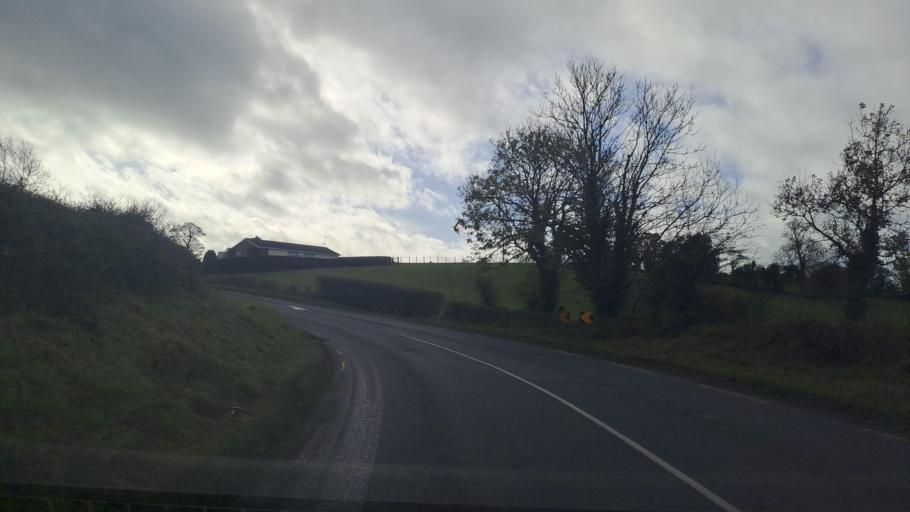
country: IE
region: Ulster
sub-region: County Monaghan
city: Monaghan
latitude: 54.1611
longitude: -7.0050
